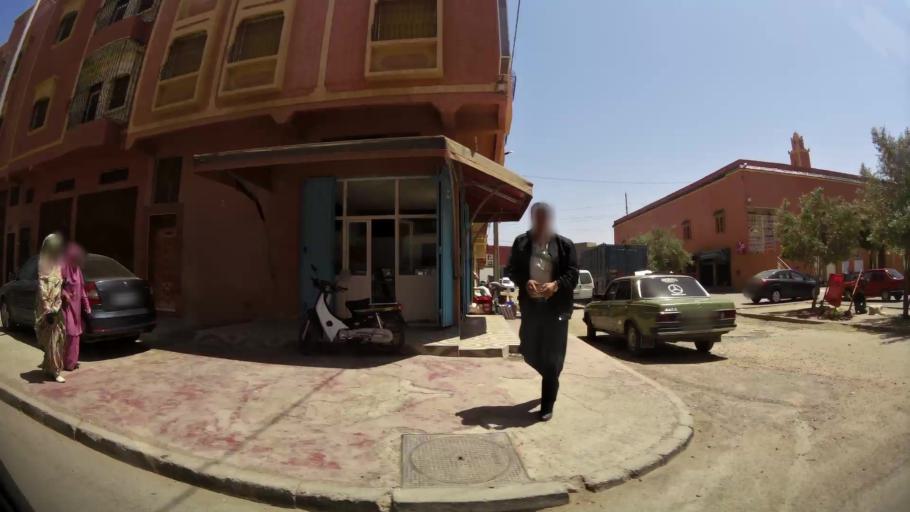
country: MA
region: Souss-Massa-Draa
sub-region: Inezgane-Ait Mellou
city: Inezgane
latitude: 30.3311
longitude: -9.4975
